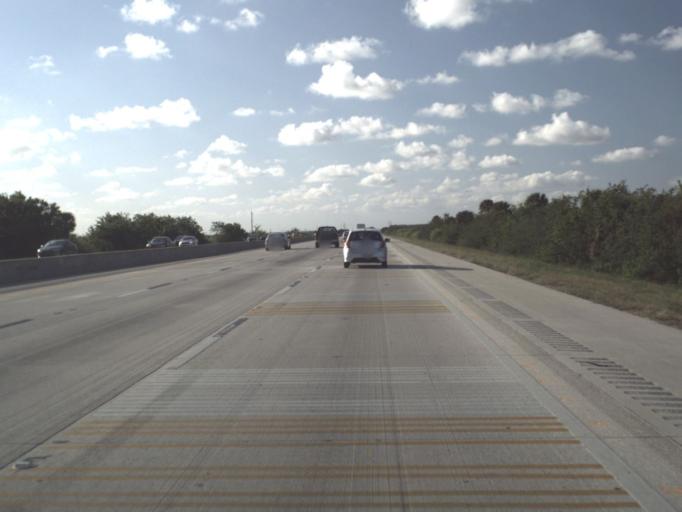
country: US
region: Florida
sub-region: Brevard County
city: Cocoa West
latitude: 28.3086
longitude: -80.7608
